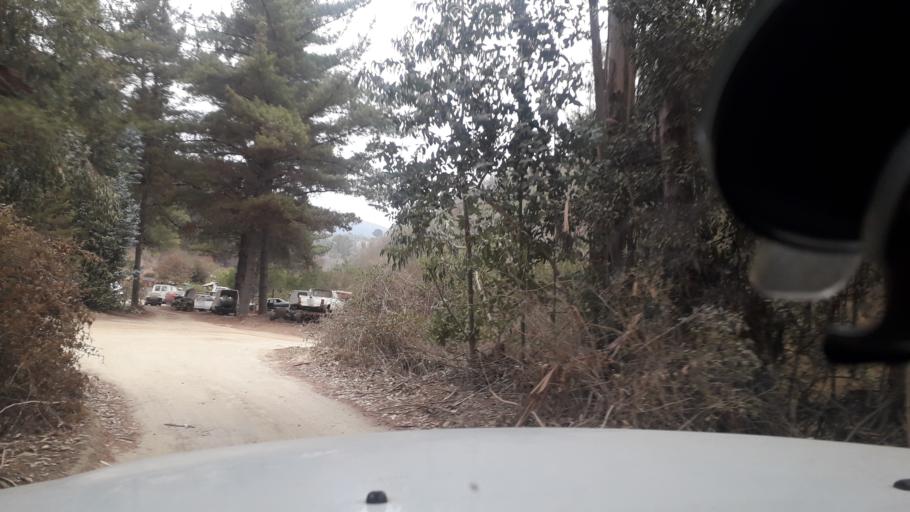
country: CL
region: Valparaiso
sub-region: Provincia de Valparaiso
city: Valparaiso
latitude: -33.1159
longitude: -71.6432
